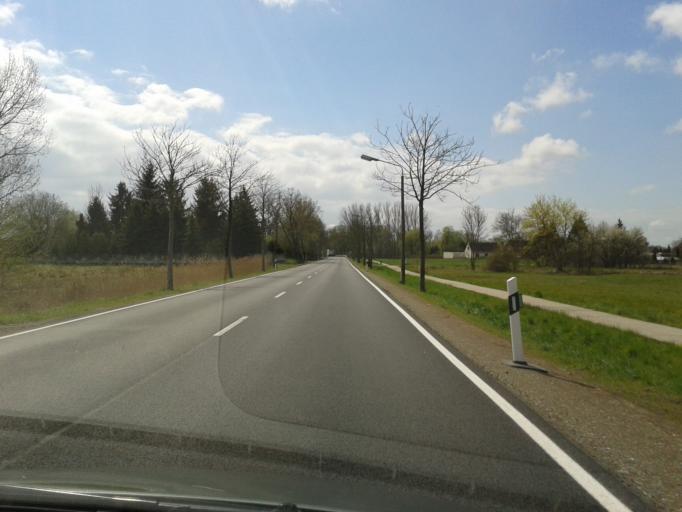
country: DE
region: Lower Saxony
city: Lubbow
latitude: 52.8835
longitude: 11.1731
